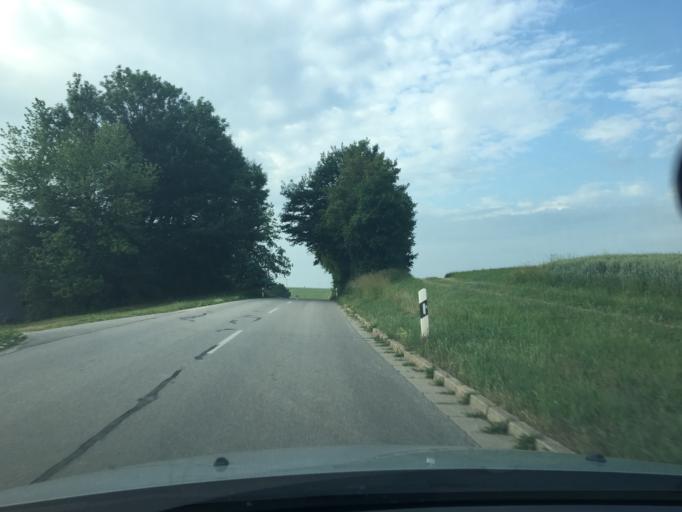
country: DE
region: Bavaria
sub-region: Lower Bavaria
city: Furth
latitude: 48.3965
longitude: 12.3549
